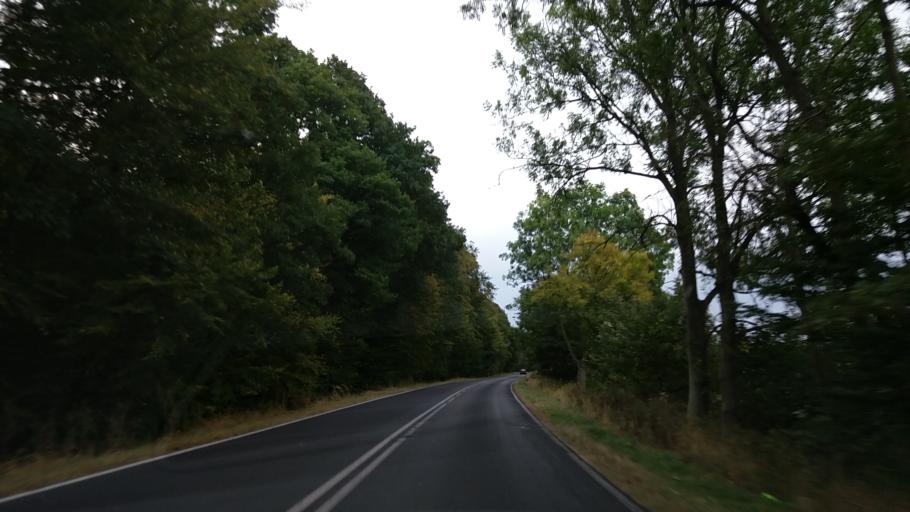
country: PL
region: West Pomeranian Voivodeship
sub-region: Powiat mysliborski
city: Barlinek
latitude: 52.9548
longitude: 15.1833
